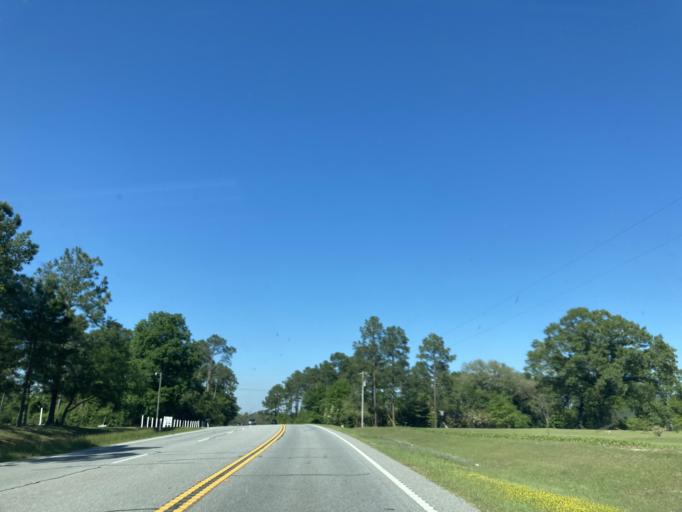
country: US
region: Georgia
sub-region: Baker County
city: Newton
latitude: 31.2955
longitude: -84.3483
